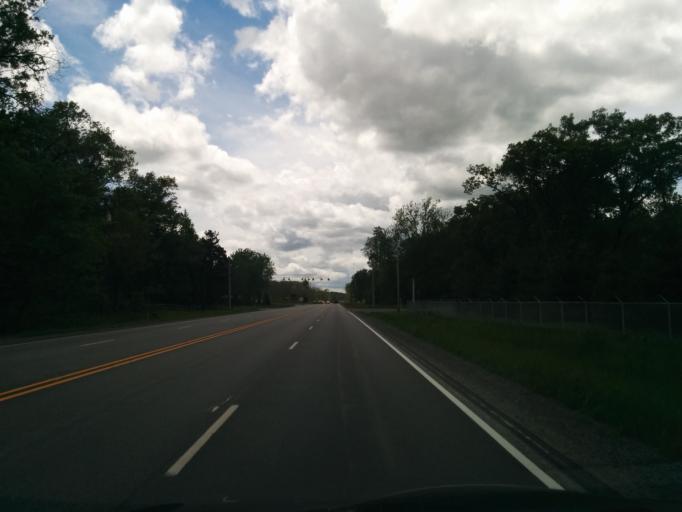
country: US
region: Indiana
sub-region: LaPorte County
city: Michigan City
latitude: 41.6737
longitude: -86.9700
